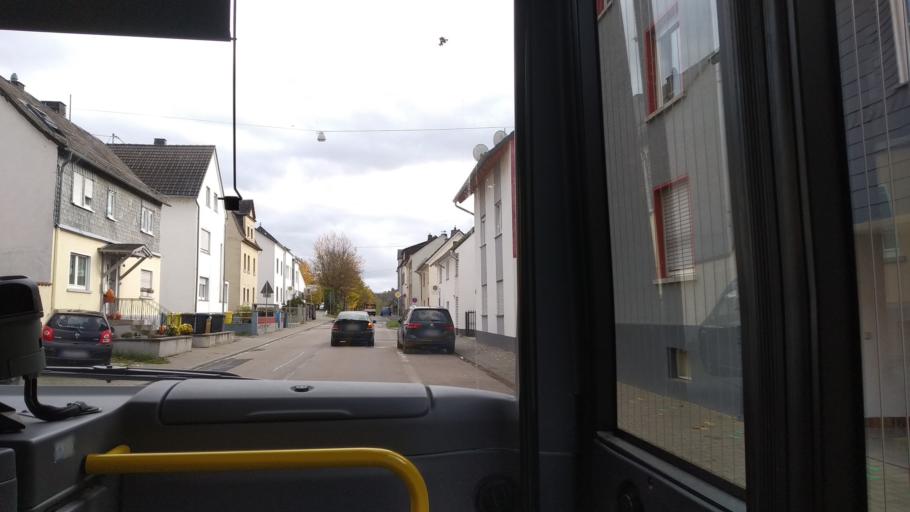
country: DE
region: Rheinland-Pfalz
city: Diez
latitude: 50.3678
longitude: 8.0290
